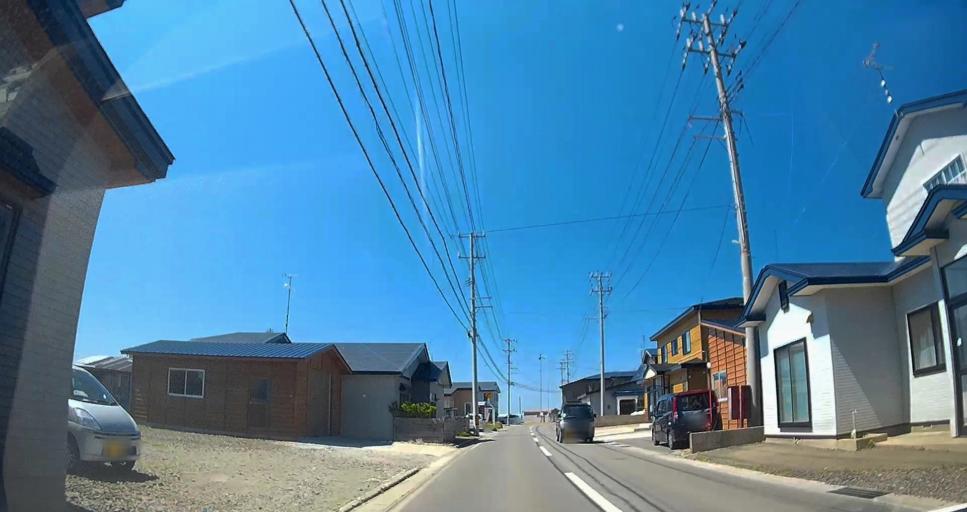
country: JP
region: Hokkaido
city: Hakodate
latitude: 41.4977
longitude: 140.9087
